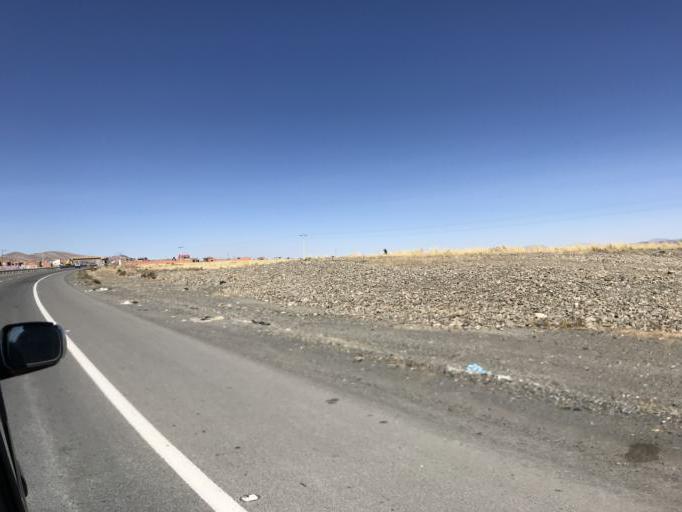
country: BO
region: La Paz
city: Batallas
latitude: -16.3241
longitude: -68.4293
